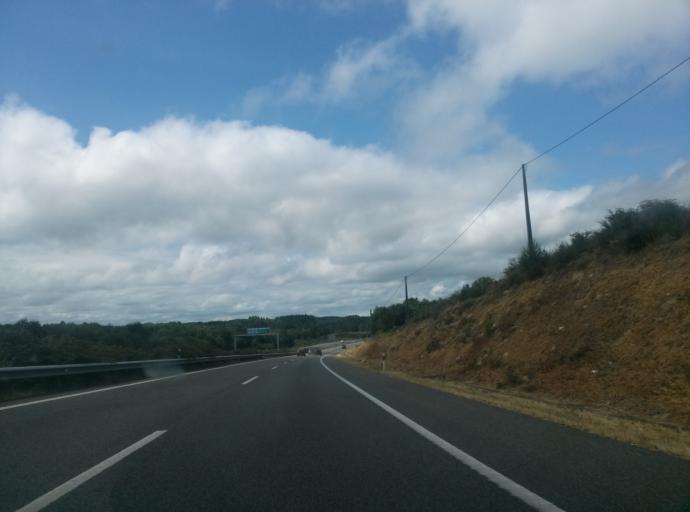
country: ES
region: Galicia
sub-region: Provincia de Lugo
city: Lugo
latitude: 43.0644
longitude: -7.5696
